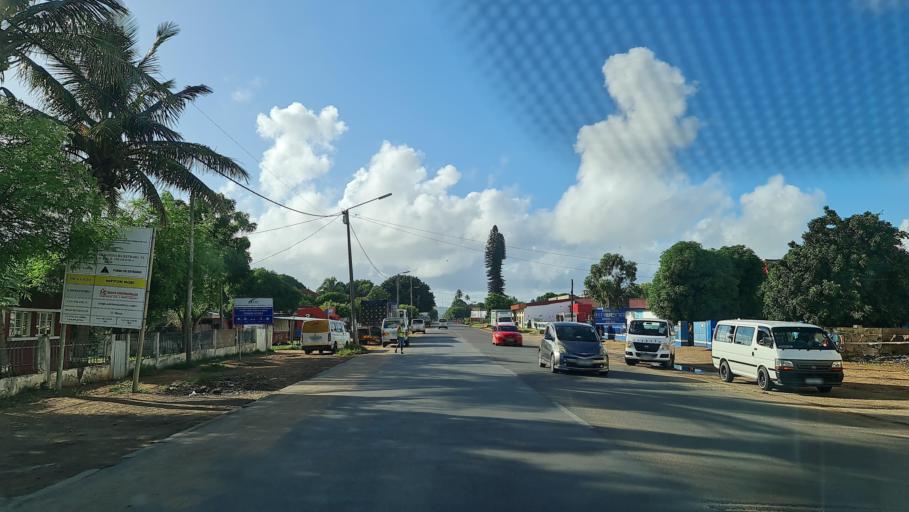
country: MZ
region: Gaza
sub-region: Xai-Xai District
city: Xai-Xai
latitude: -25.0300
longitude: 33.6331
